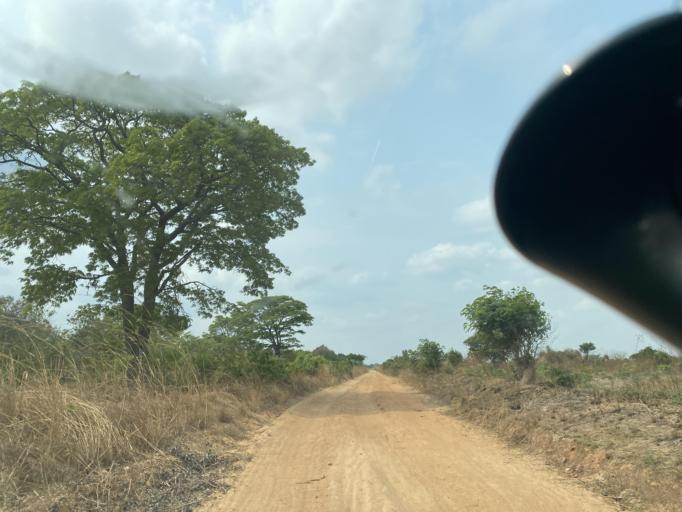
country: ZM
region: Lusaka
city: Lusaka
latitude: -15.1367
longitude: 28.3681
